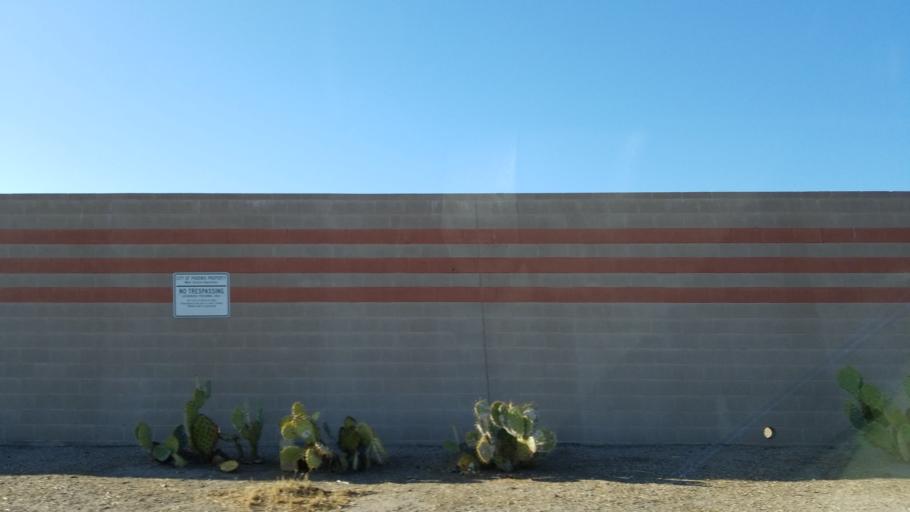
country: US
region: Arizona
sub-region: Maricopa County
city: Phoenix
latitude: 33.4224
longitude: -112.1117
